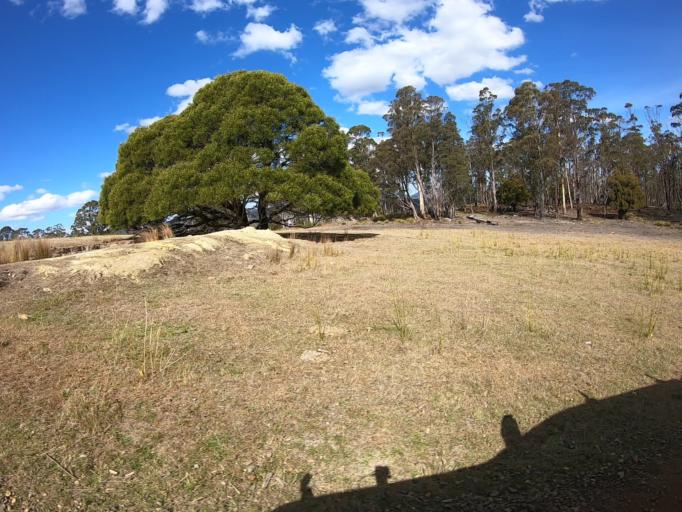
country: AU
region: Tasmania
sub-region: Brighton
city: Bridgewater
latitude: -42.4967
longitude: 147.4226
